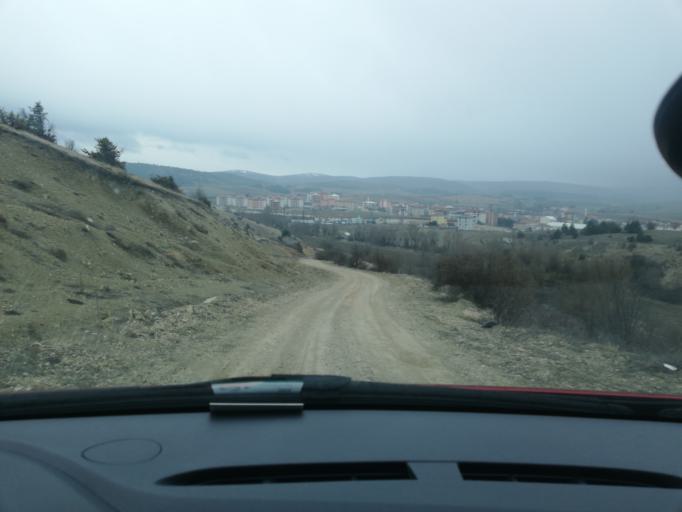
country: TR
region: Kastamonu
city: Seydiler
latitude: 41.6241
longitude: 33.7254
